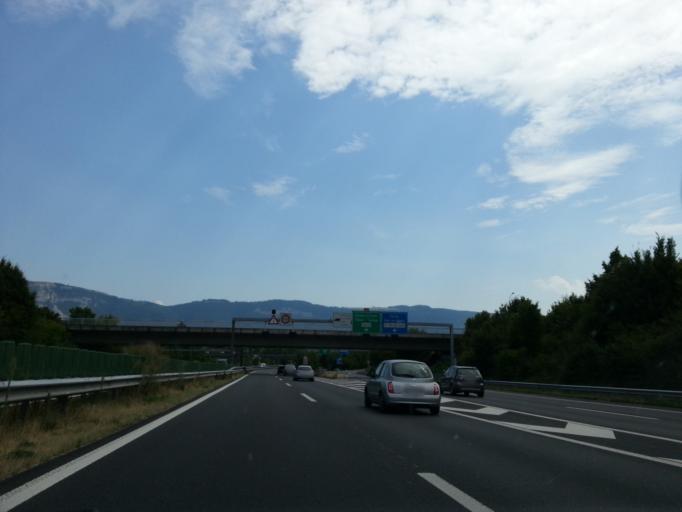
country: CH
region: Geneva
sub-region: Geneva
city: Confignon
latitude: 46.1669
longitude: 6.0968
